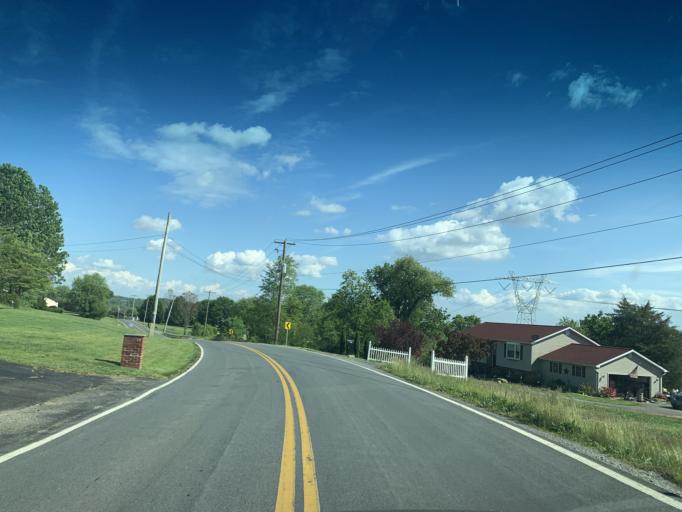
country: US
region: Maryland
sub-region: Cecil County
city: Rising Sun
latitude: 39.7007
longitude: -76.1448
